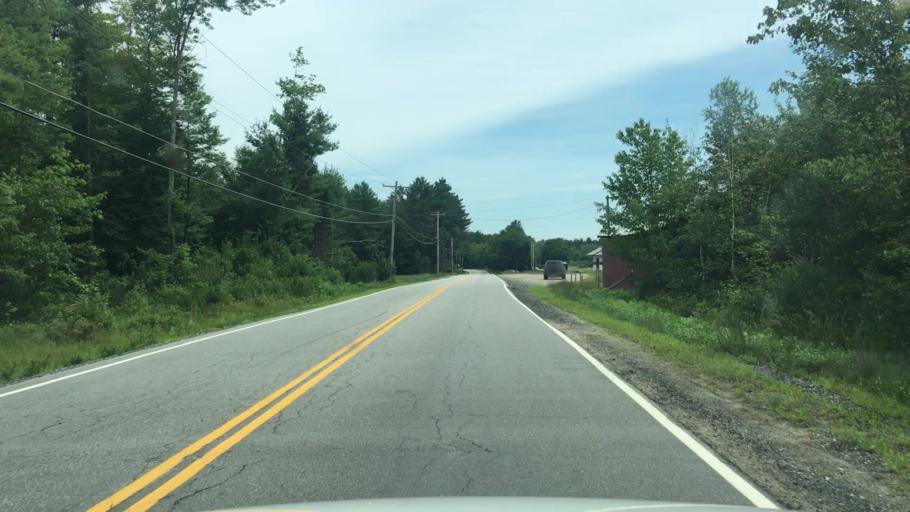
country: US
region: New Hampshire
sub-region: Grafton County
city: Rumney
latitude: 43.7791
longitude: -71.7547
